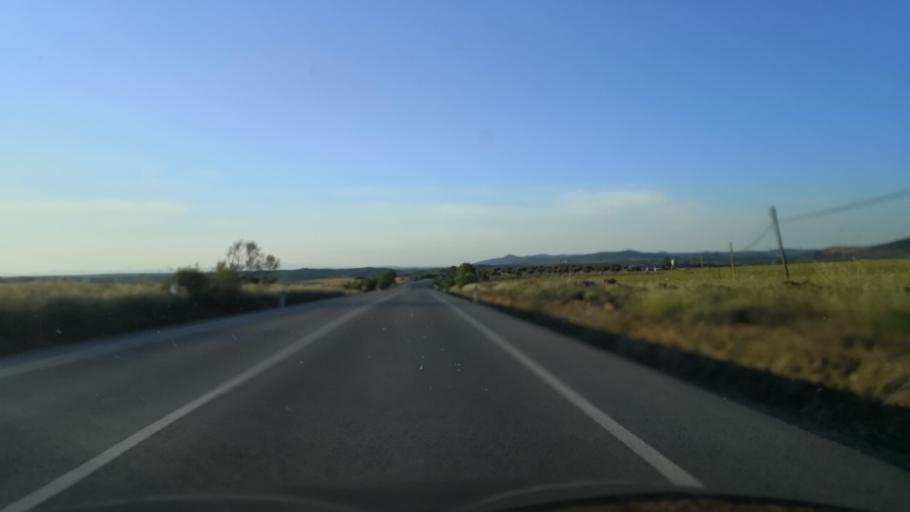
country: ES
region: Extremadura
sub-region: Provincia de Caceres
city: Valencia de Alcantara
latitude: 39.4426
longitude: -7.2248
